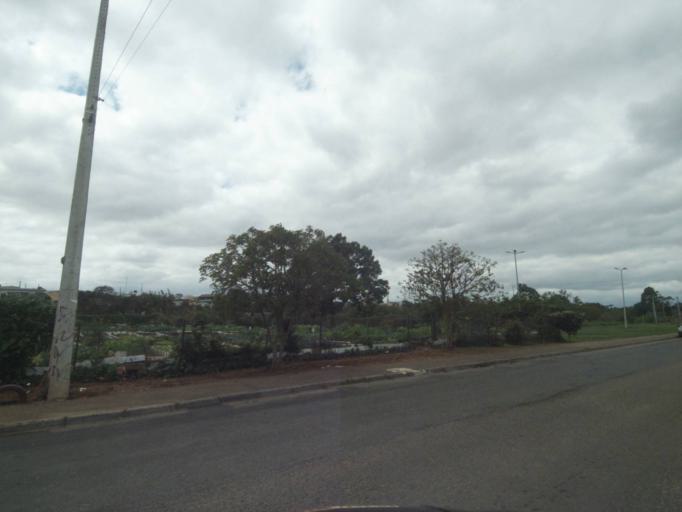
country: BR
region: Parana
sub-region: Sao Jose Dos Pinhais
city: Sao Jose dos Pinhais
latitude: -25.5539
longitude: -49.2603
